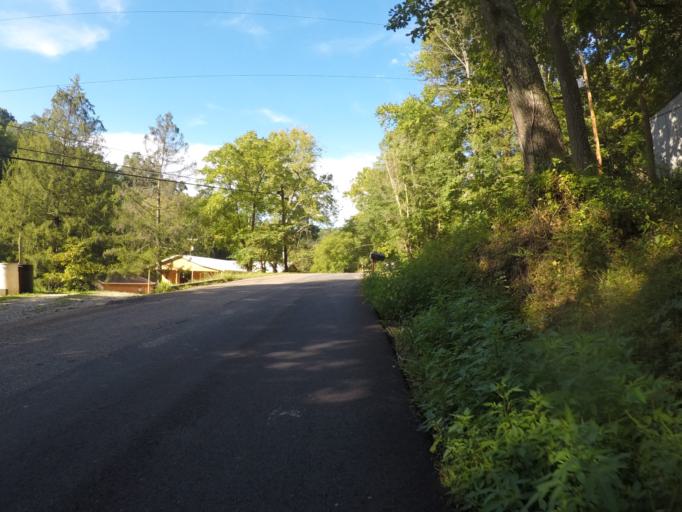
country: US
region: West Virginia
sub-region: Cabell County
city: Huntington
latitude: 38.4514
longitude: -82.4682
